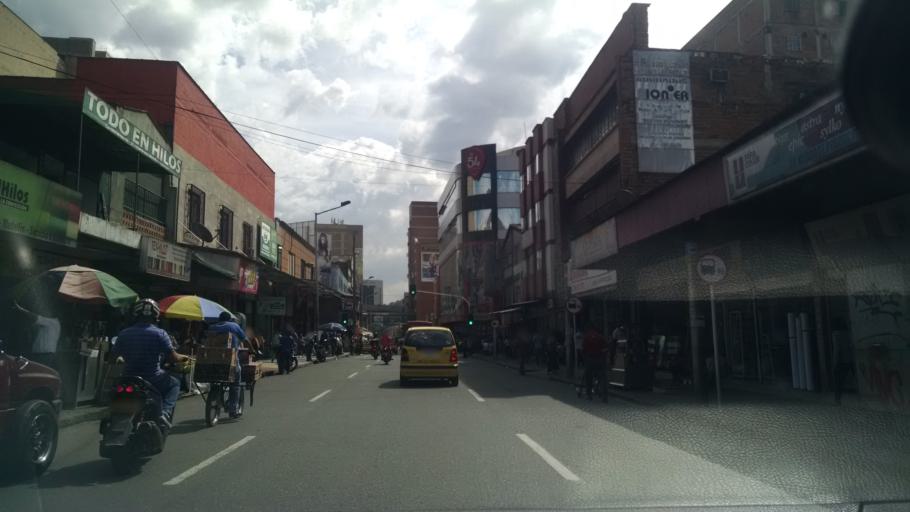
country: CO
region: Antioquia
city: Medellin
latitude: 6.2507
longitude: -75.5716
